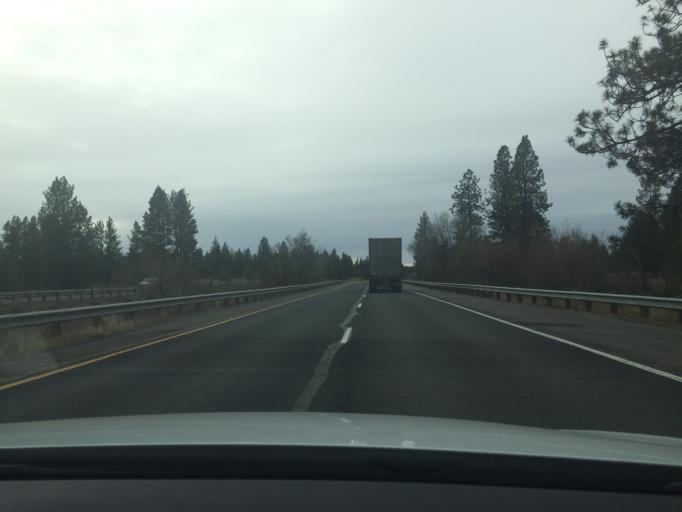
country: US
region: Washington
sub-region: Spokane County
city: Medical Lake
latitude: 47.5350
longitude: -117.6461
